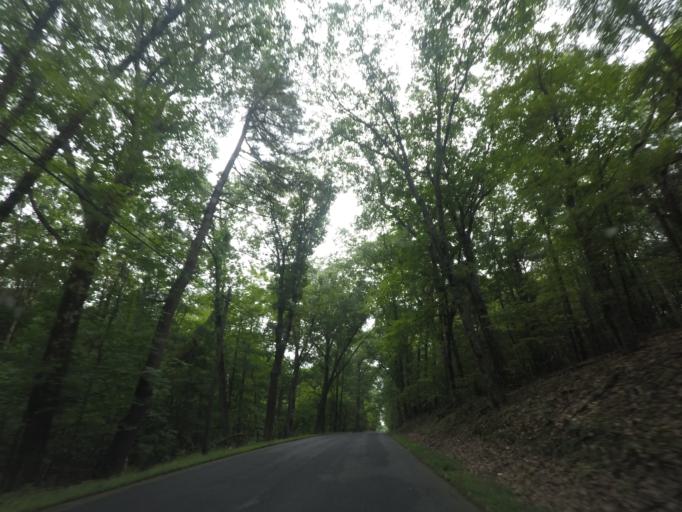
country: US
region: New York
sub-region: Rensselaer County
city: Nassau
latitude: 42.5021
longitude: -73.6057
